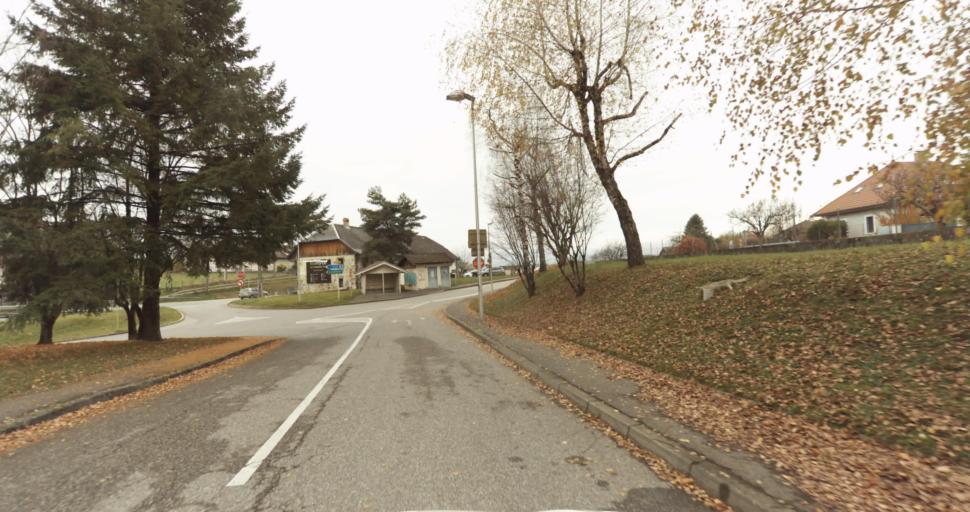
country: FR
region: Rhone-Alpes
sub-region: Departement de la Haute-Savoie
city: Alby-sur-Cheran
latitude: 45.8201
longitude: 6.0091
